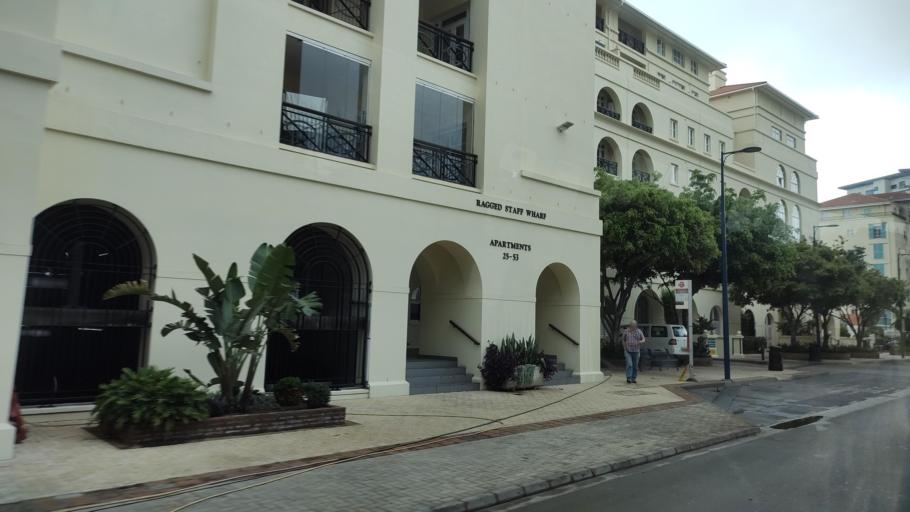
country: GI
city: Gibraltar
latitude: 36.1353
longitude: -5.3544
